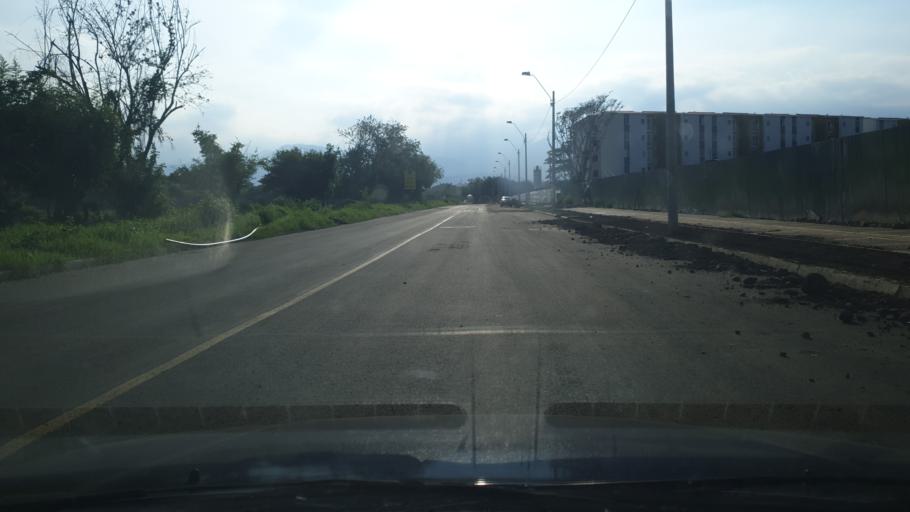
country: CO
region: Valle del Cauca
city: Jamundi
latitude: 3.3443
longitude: -76.5150
